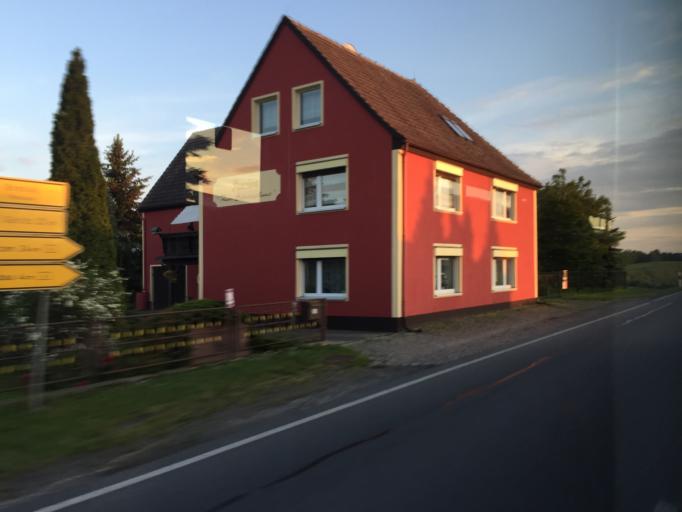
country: DE
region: Saxony
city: Lobau
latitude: 51.1136
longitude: 14.7148
